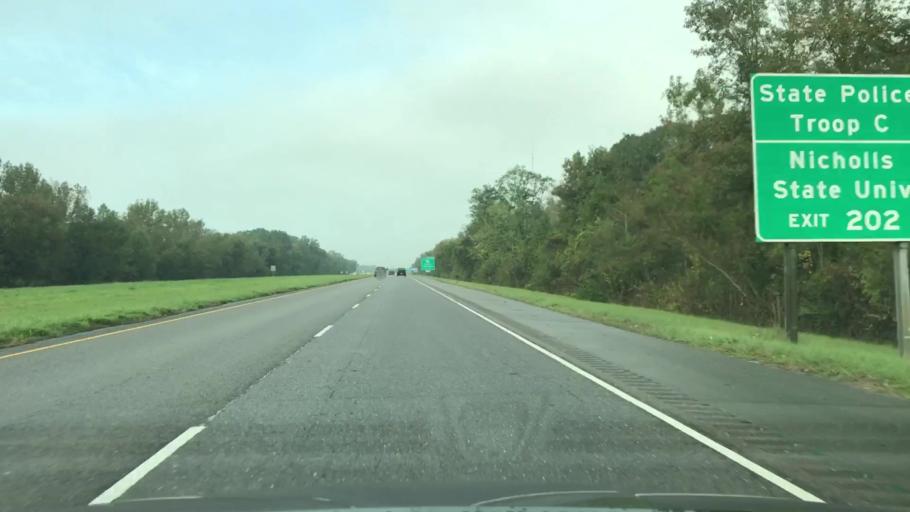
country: US
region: Louisiana
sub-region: Terrebonne Parish
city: Gray
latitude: 29.6813
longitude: -90.7677
